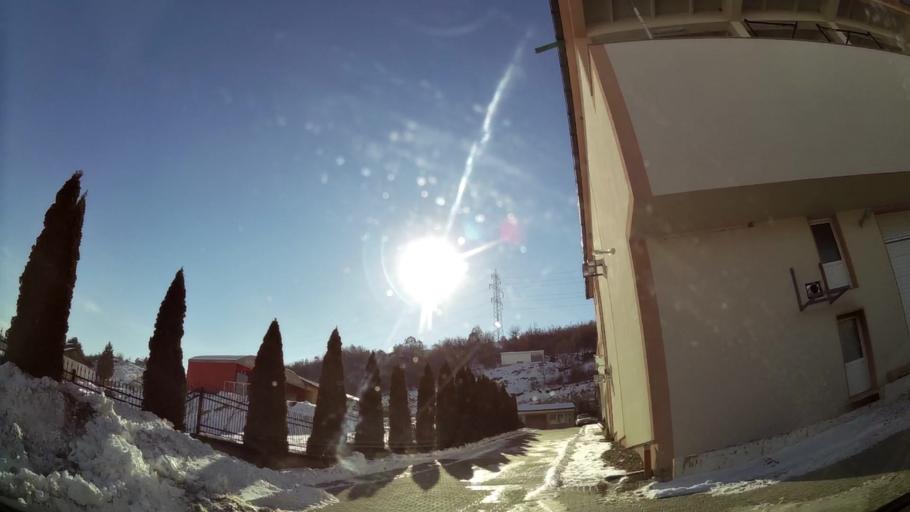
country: MK
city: Ljubin
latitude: 42.0035
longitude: 21.3005
